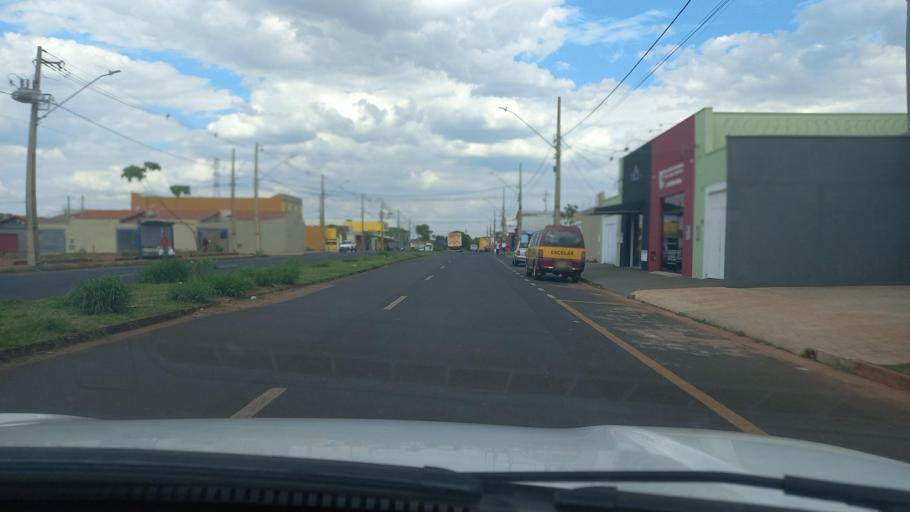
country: BR
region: Minas Gerais
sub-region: Uberaba
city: Uberaba
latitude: -19.7580
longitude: -47.9918
